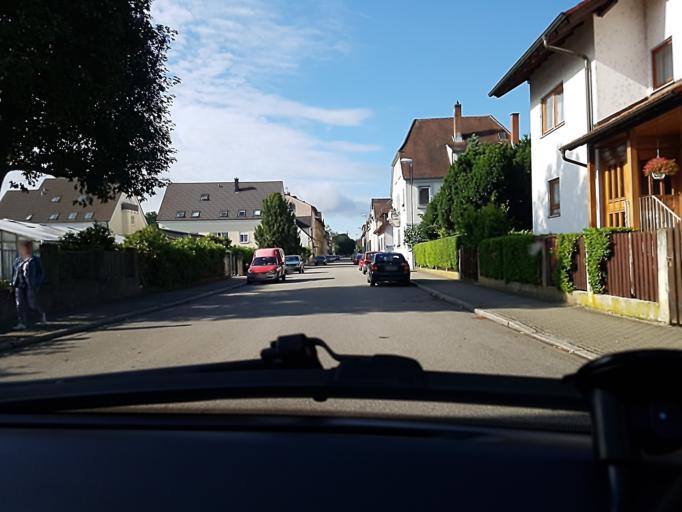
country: DE
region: Baden-Wuerttemberg
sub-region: Freiburg Region
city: Kehl
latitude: 48.5696
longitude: 7.8178
